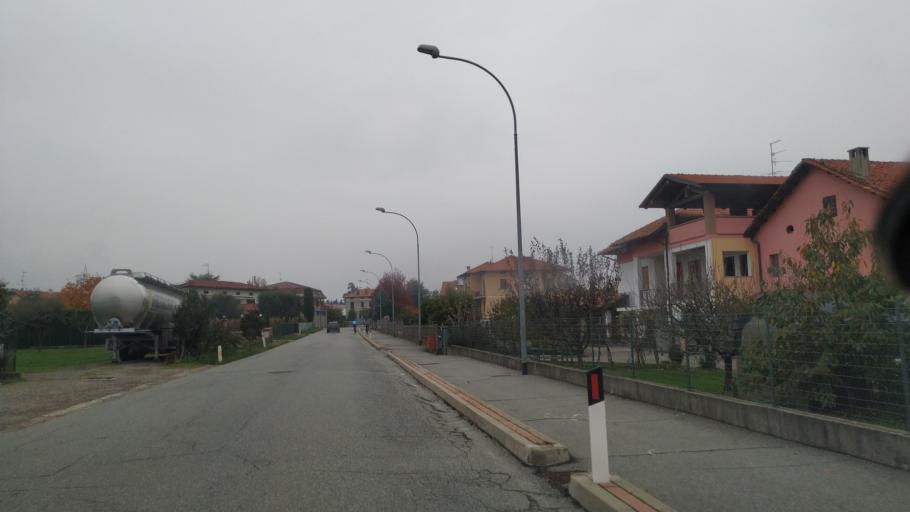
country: IT
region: Piedmont
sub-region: Provincia di Biella
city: Lessona
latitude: 45.5798
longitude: 8.2000
